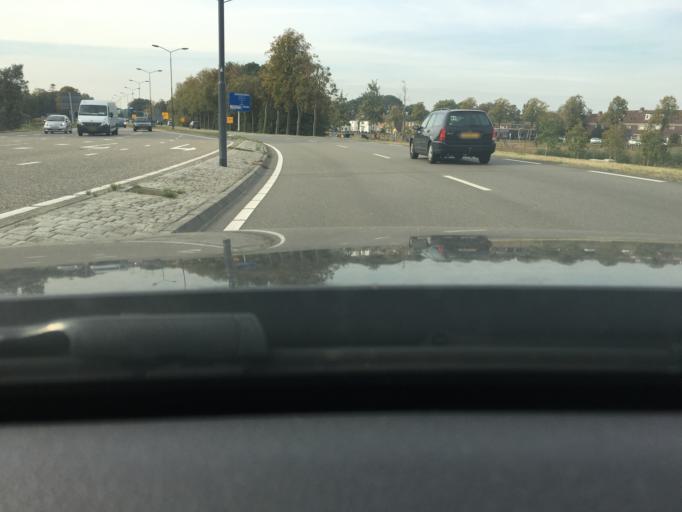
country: NL
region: North Brabant
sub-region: Gemeente 's-Hertogenbosch
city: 's-Hertogenbosch
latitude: 51.6860
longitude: 5.2788
